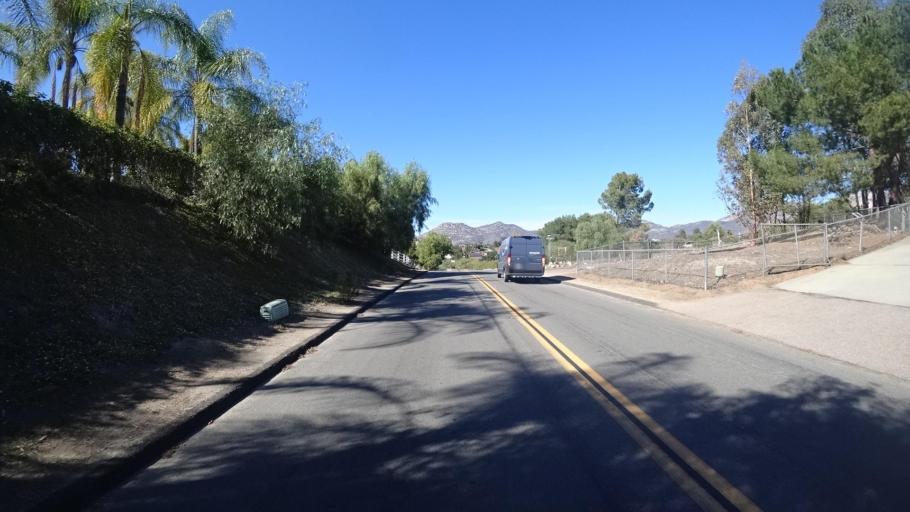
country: US
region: California
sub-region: San Diego County
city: Harbison Canyon
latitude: 32.8637
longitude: -116.8606
